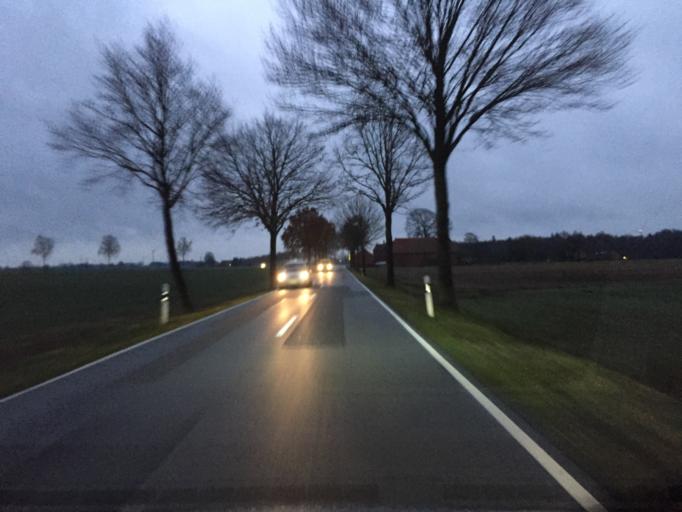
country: DE
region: Lower Saxony
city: Sudwalde
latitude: 52.7725
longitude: 8.8325
